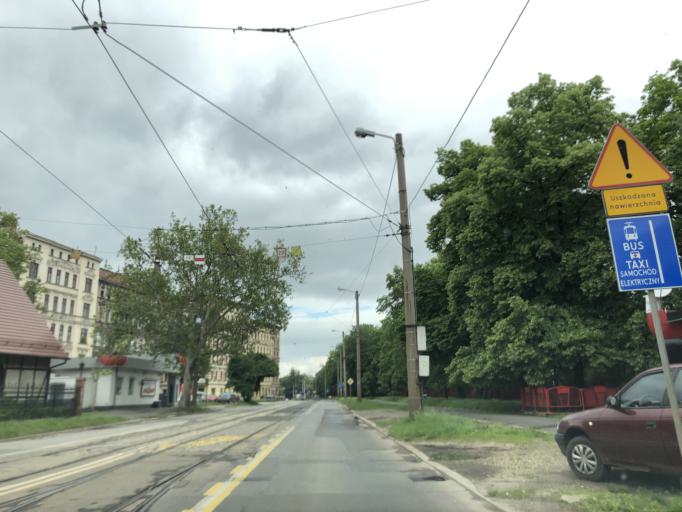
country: PL
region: Lower Silesian Voivodeship
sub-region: Powiat wroclawski
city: Wroclaw
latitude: 51.1229
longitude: 17.0302
